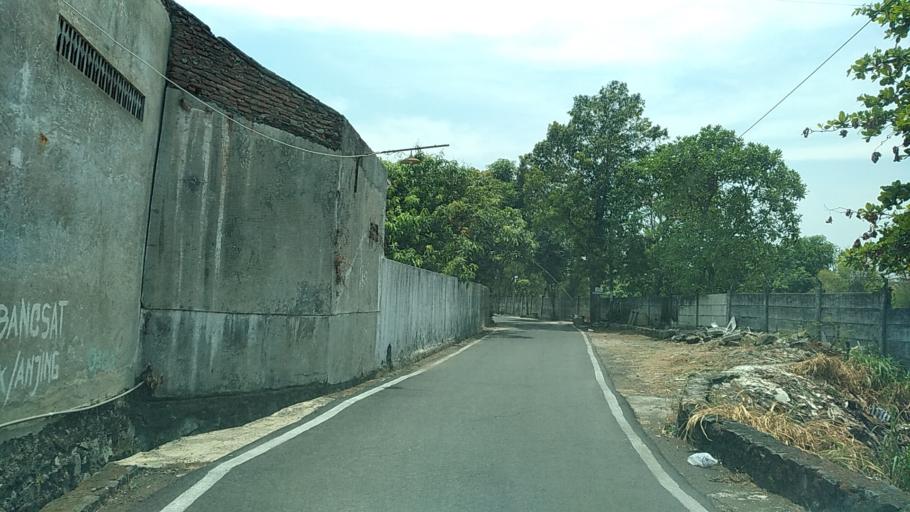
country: ID
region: Central Java
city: Semarang
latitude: -7.0583
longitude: 110.4191
